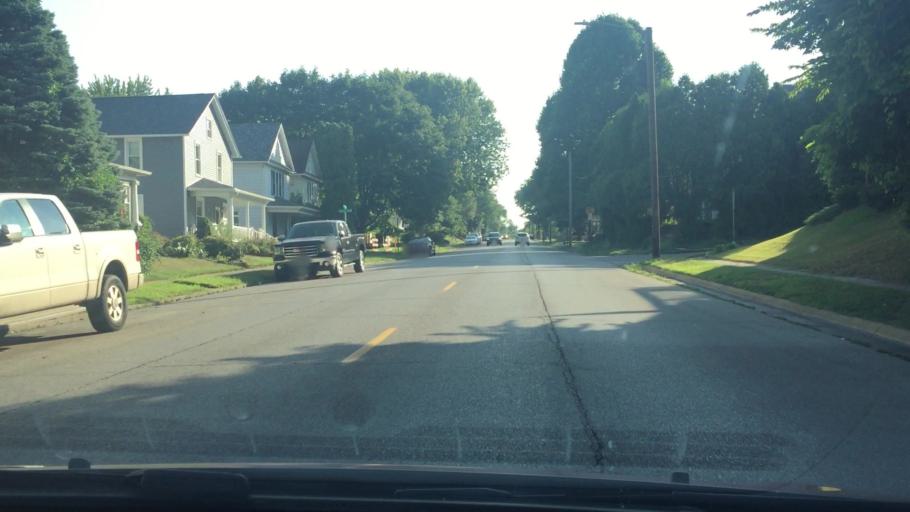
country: US
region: Iowa
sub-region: Muscatine County
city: Muscatine
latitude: 41.4241
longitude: -91.0539
